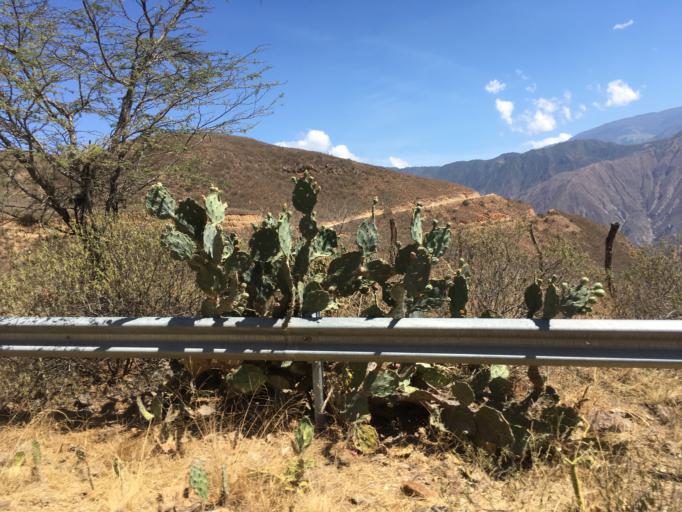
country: CO
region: Santander
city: Aratoca
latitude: 6.7909
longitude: -72.9967
